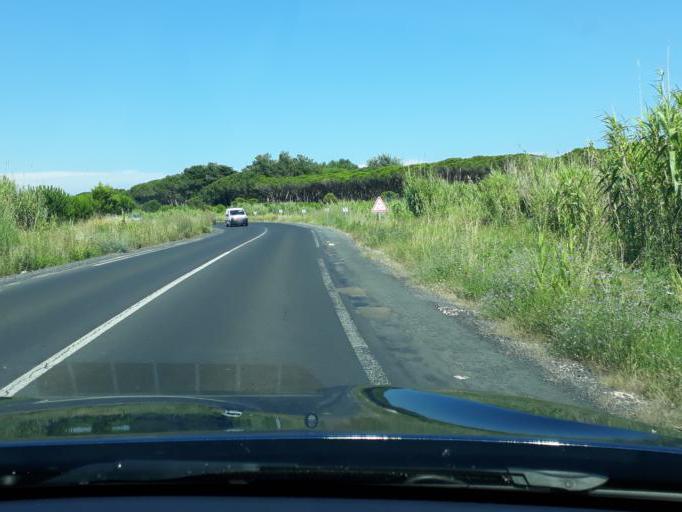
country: FR
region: Languedoc-Roussillon
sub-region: Departement de l'Herault
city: Marseillan
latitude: 43.3395
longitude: 3.5740
